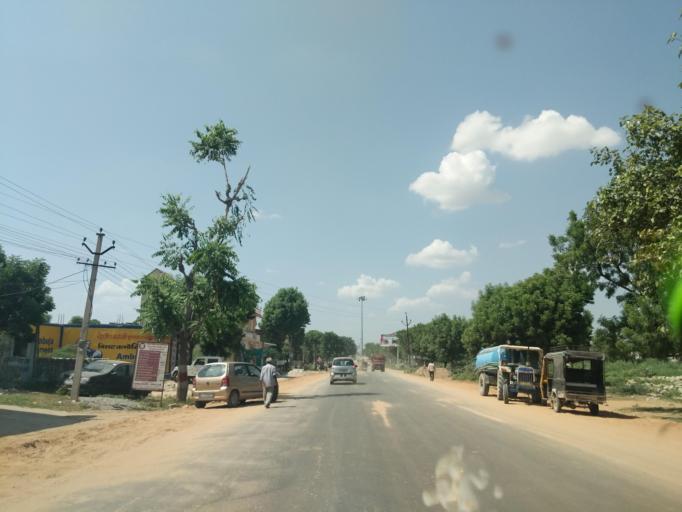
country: IN
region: Rajasthan
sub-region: Nagaur
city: Makrana
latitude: 27.0275
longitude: 74.7539
